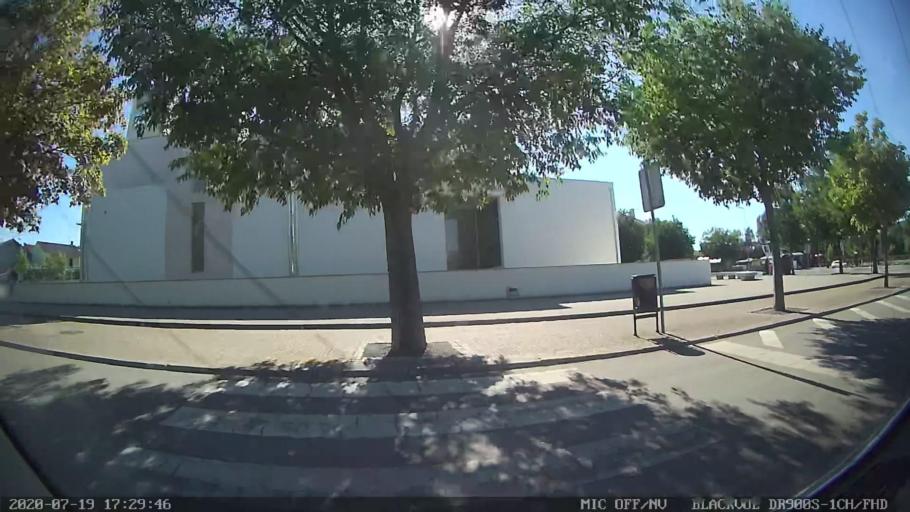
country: PT
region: Braganca
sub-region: Braganca Municipality
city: Braganca
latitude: 41.7969
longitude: -6.7713
